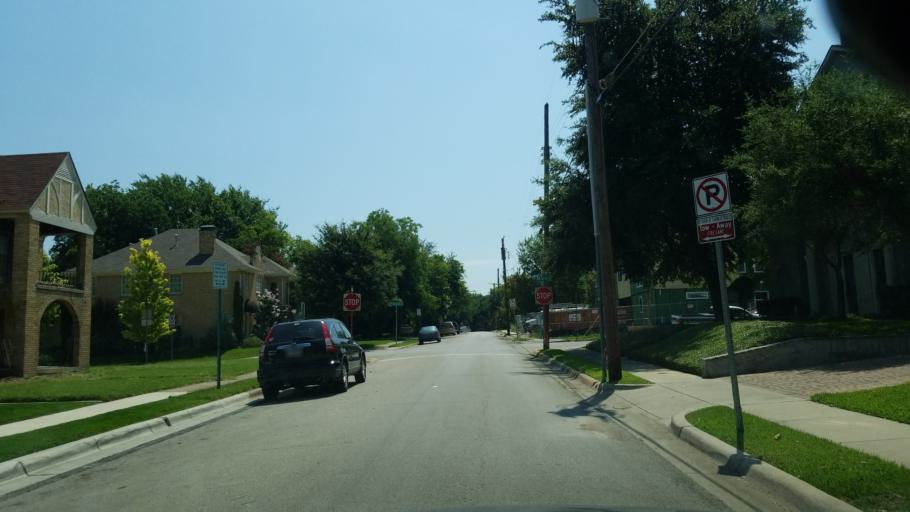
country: US
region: Texas
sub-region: Dallas County
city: University Park
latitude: 32.8476
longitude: -96.7854
